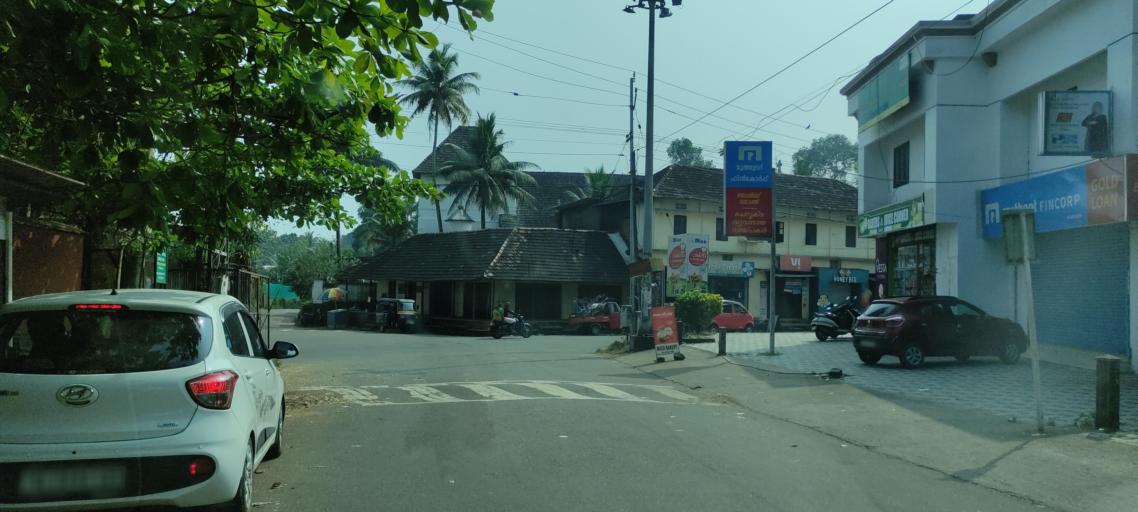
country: IN
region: Kerala
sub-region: Pattanamtitta
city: Adur
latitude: 9.2216
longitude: 76.7136
